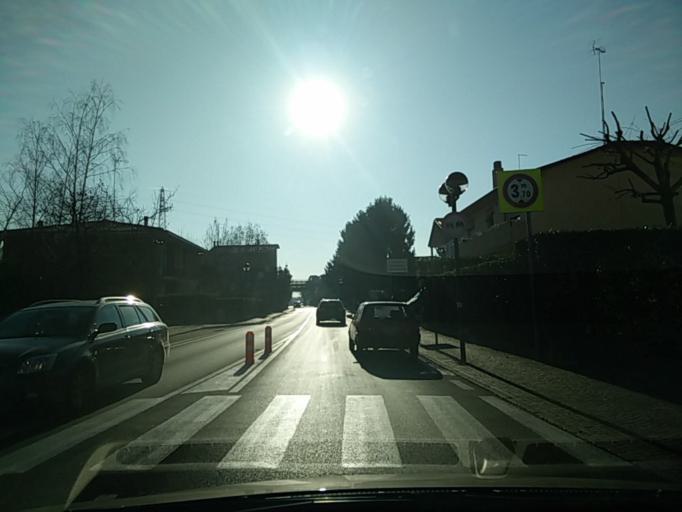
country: IT
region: Veneto
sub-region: Provincia di Treviso
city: Silea
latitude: 45.6611
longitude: 12.2922
